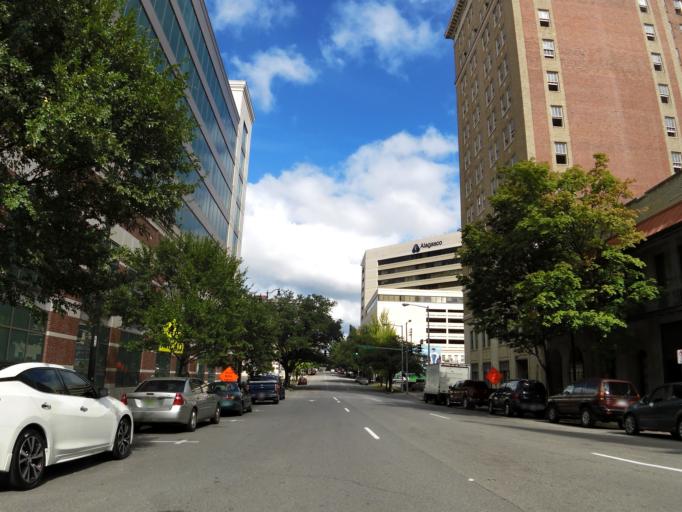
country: US
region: Alabama
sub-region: Jefferson County
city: Birmingham
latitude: 33.5180
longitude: -86.8069
